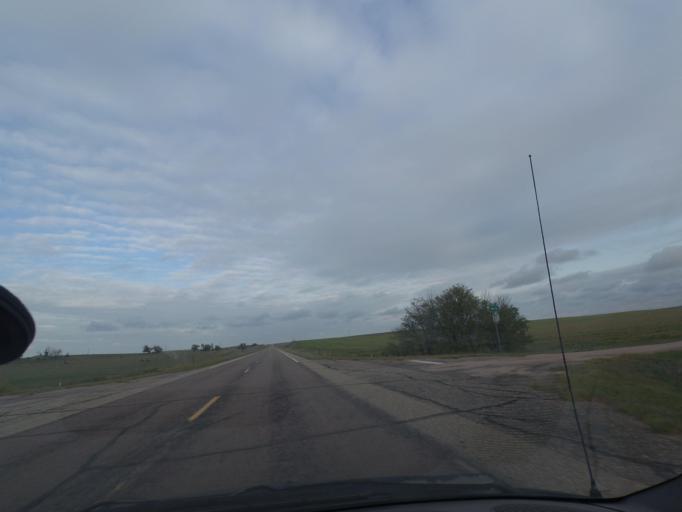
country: US
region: Colorado
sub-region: Kit Carson County
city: Burlington
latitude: 39.6580
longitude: -102.5181
